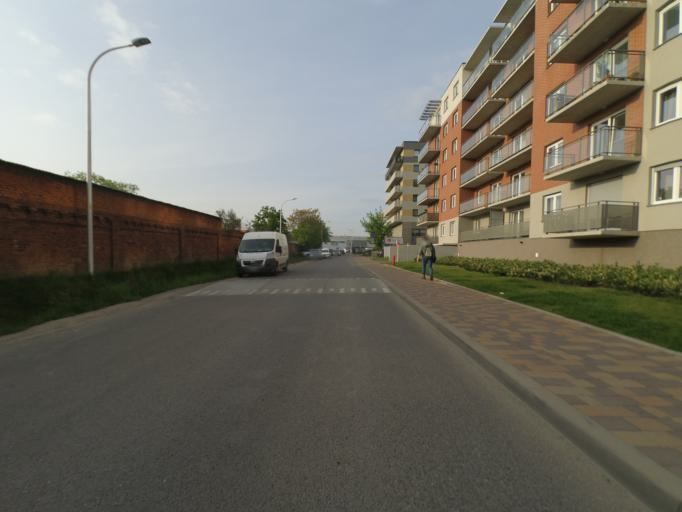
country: PL
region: Lower Silesian Voivodeship
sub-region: Powiat wroclawski
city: Wroclaw
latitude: 51.1287
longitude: 17.0401
